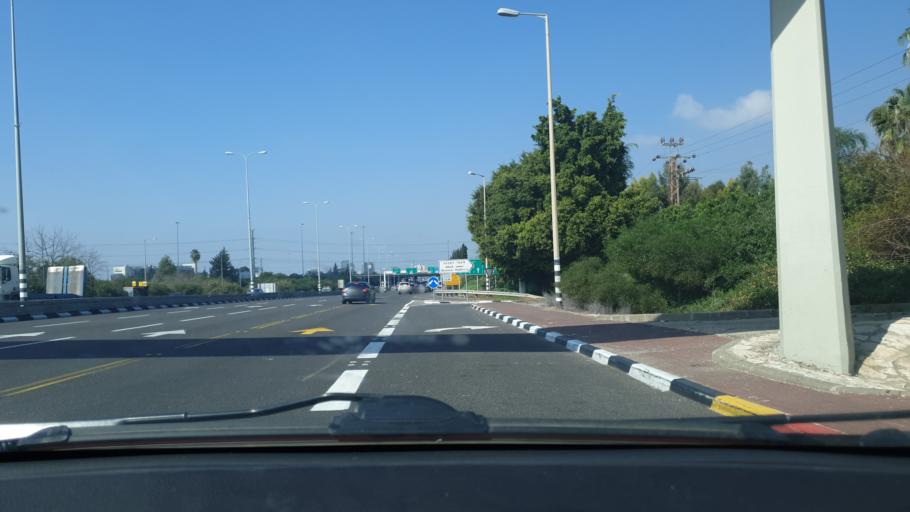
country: IL
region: Central District
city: Bet Dagan
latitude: 32.0058
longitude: 34.8178
